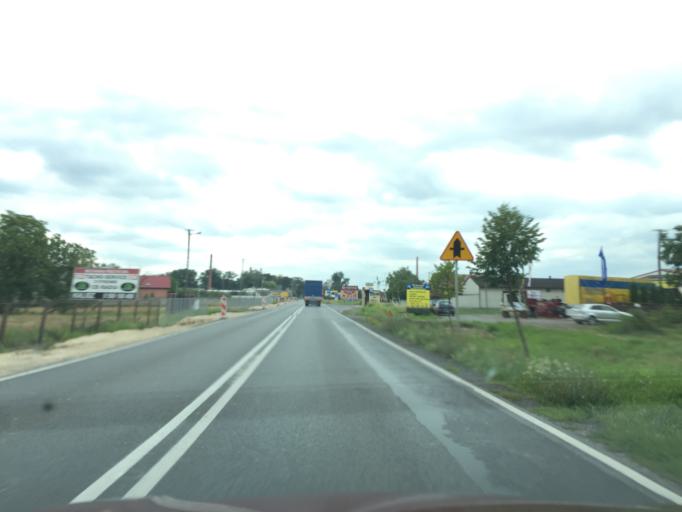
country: PL
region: Greater Poland Voivodeship
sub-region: Kalisz
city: Kalisz
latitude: 51.8005
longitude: 18.0921
